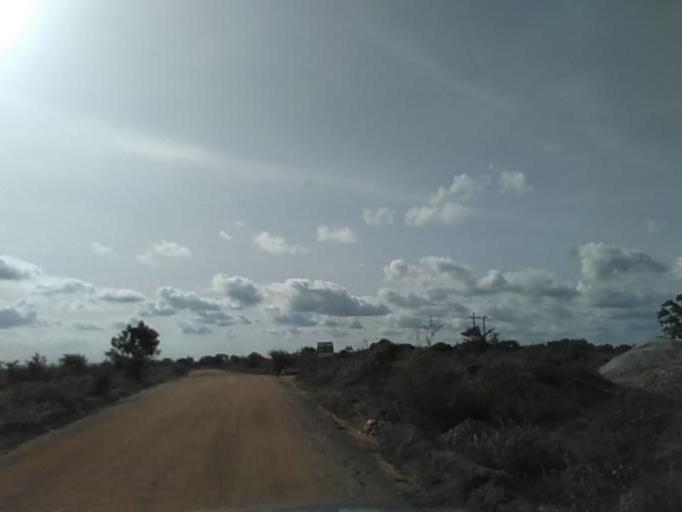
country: GH
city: Akropong
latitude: 6.0925
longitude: 0.2618
